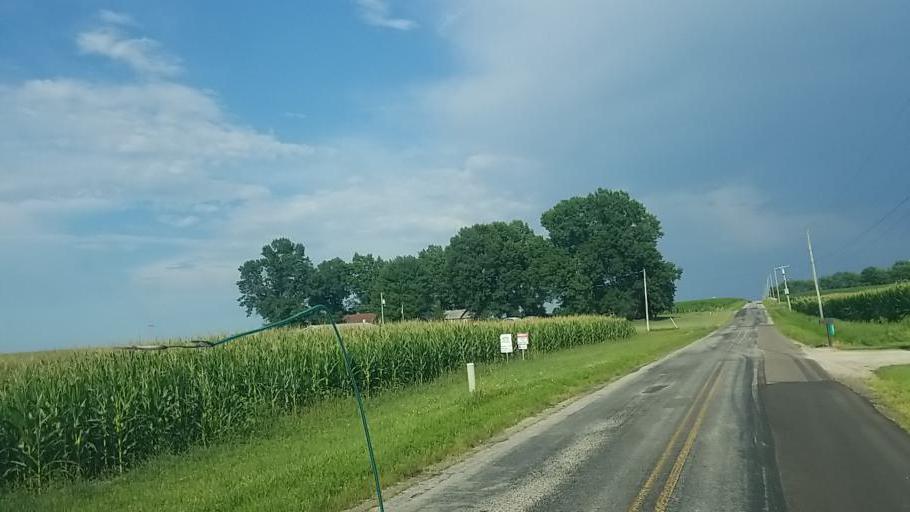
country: US
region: Ohio
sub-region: Wayne County
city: Smithville
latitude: 40.9164
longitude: -81.8615
